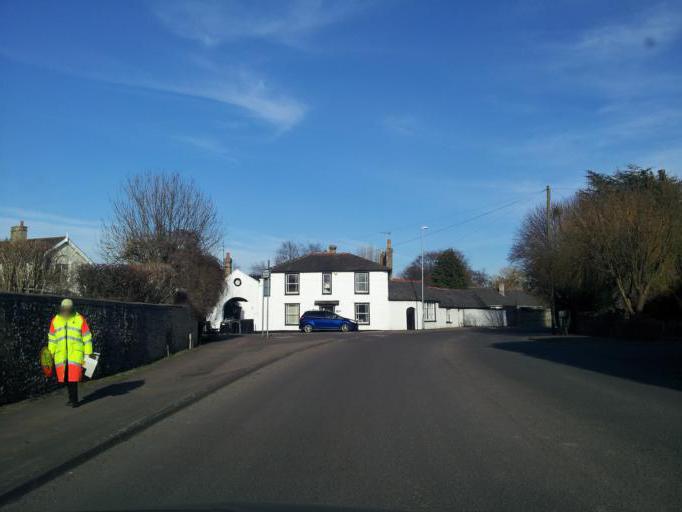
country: GB
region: England
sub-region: Cambridgeshire
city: Melbourn
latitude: 52.0859
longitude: 0.0202
